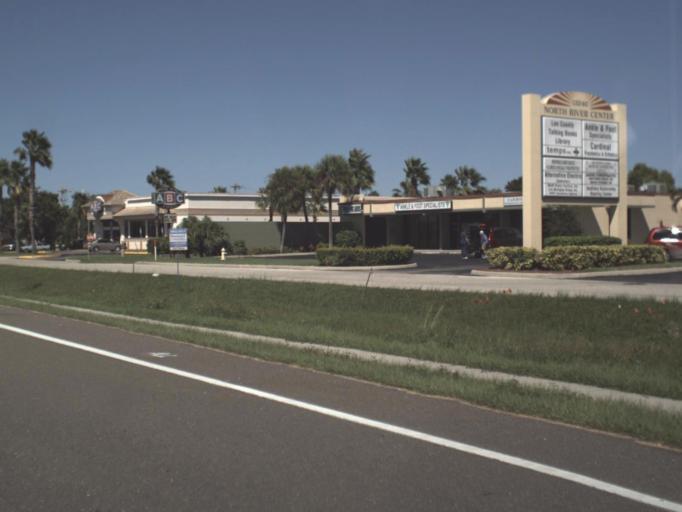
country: US
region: Florida
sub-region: Lee County
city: North Fort Myers
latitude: 26.6610
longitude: -81.8844
